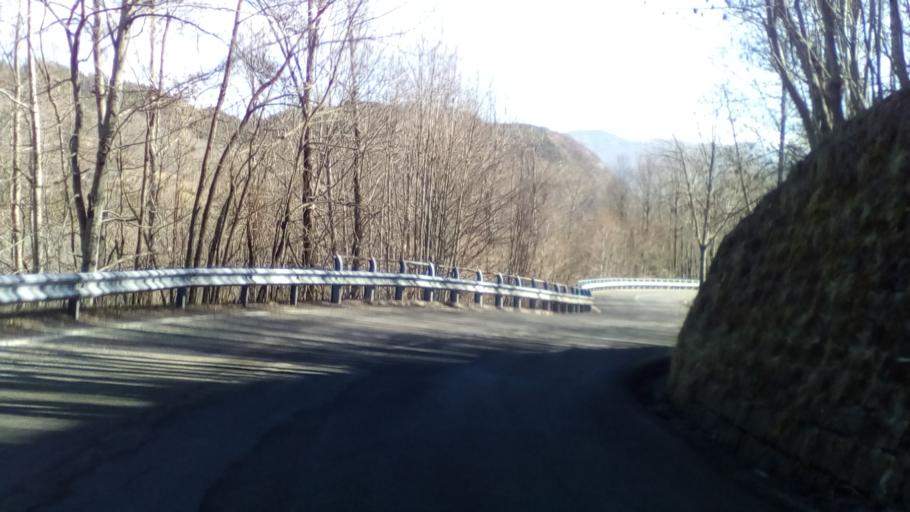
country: IT
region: Emilia-Romagna
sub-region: Provincia di Modena
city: Pievepelago
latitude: 44.1901
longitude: 10.5567
